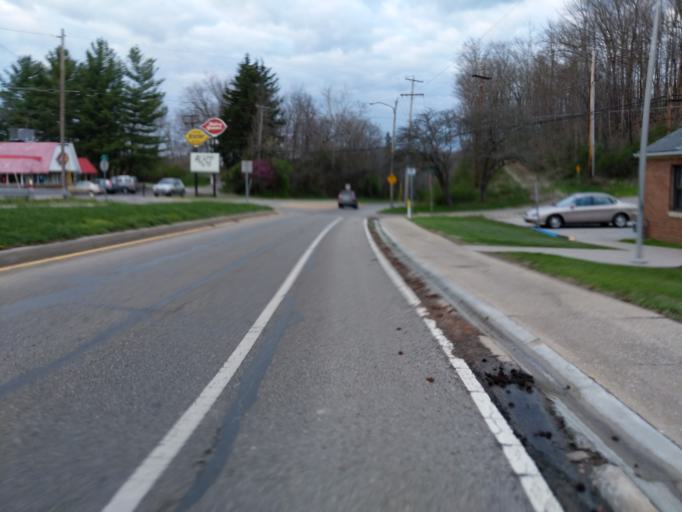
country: US
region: Ohio
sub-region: Athens County
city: Athens
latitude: 39.3391
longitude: -82.1041
